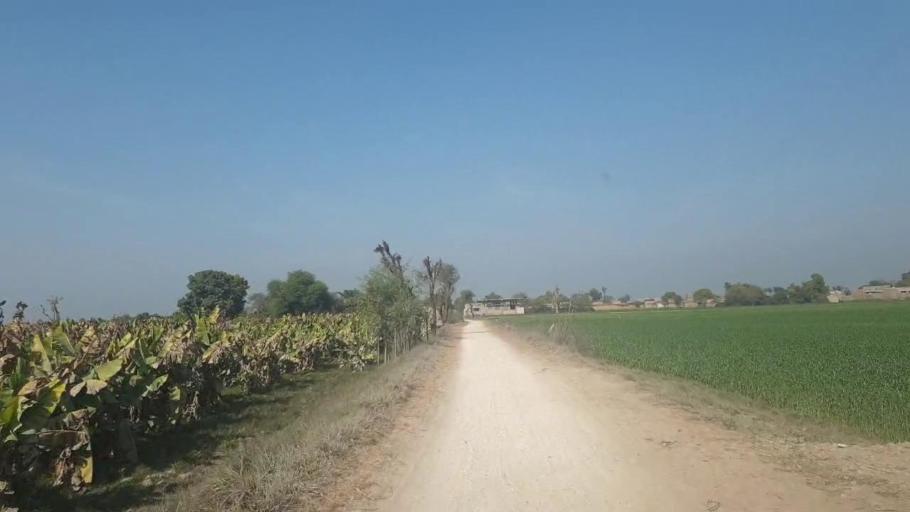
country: PK
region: Sindh
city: Sakrand
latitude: 26.0774
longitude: 68.4187
